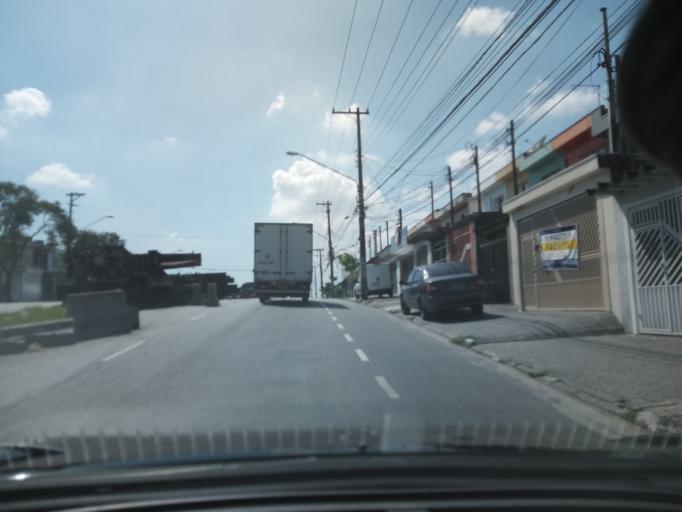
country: BR
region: Sao Paulo
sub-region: Sao Bernardo Do Campo
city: Sao Bernardo do Campo
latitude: -23.7176
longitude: -46.5354
